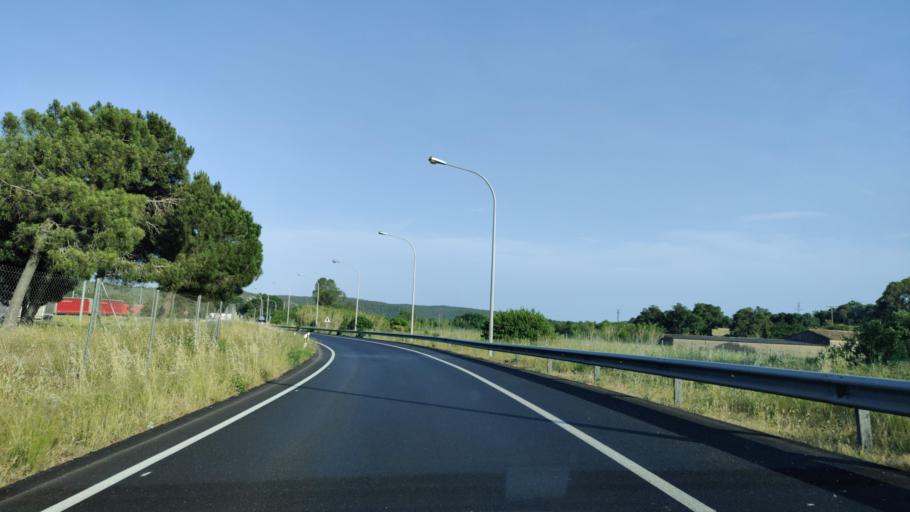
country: ES
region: Catalonia
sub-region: Provincia de Girona
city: la Jonquera
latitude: 42.4052
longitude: 2.8712
